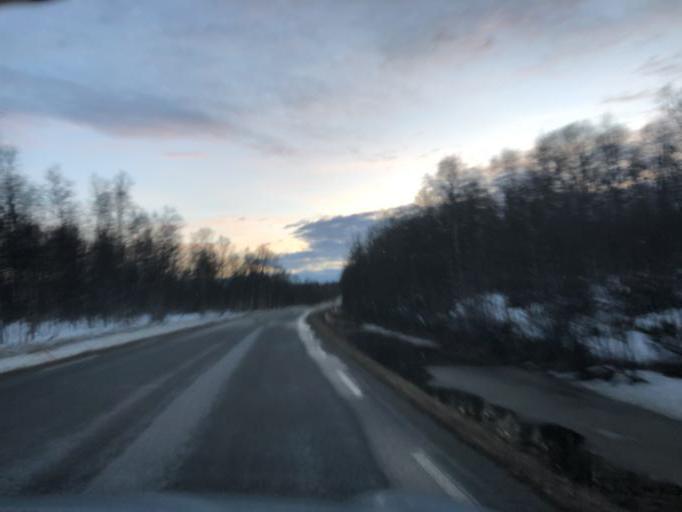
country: NO
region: Sor-Trondelag
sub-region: Tydal
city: Aas
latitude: 62.6722
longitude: 11.8243
